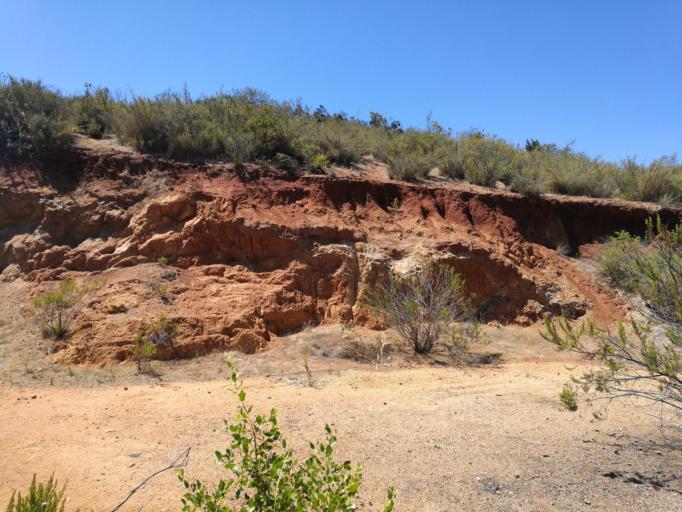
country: CL
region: Valparaiso
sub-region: Provincia de Valparaiso
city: Valparaiso
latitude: -33.0740
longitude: -71.6575
